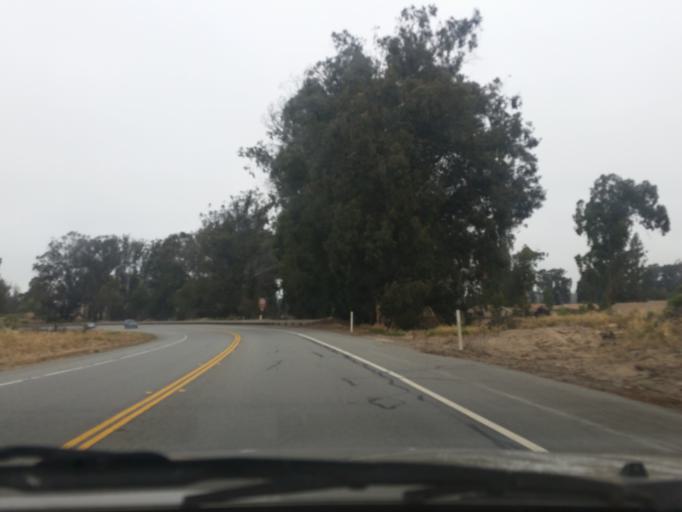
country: US
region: California
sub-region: San Luis Obispo County
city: Callender
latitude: 35.0493
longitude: -120.5928
